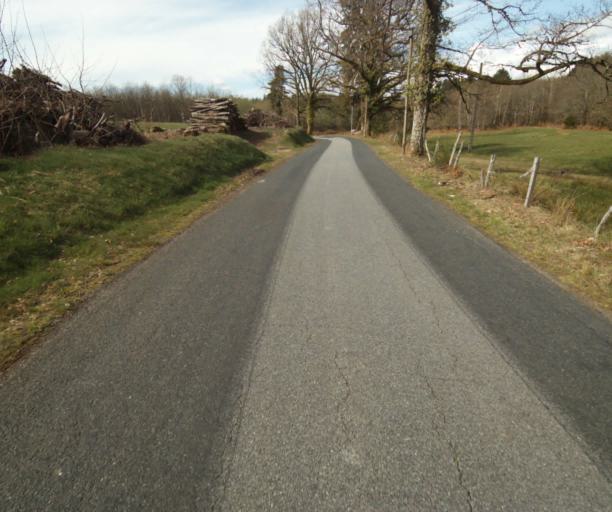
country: FR
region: Limousin
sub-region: Departement de la Correze
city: Correze
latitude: 45.3510
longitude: 1.9041
